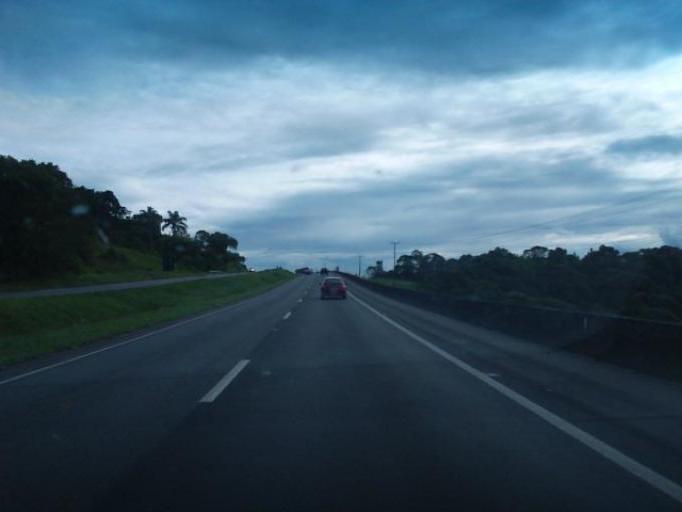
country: BR
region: Parana
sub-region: Campina Grande Do Sul
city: Campina Grande do Sul
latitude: -25.1457
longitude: -48.8583
